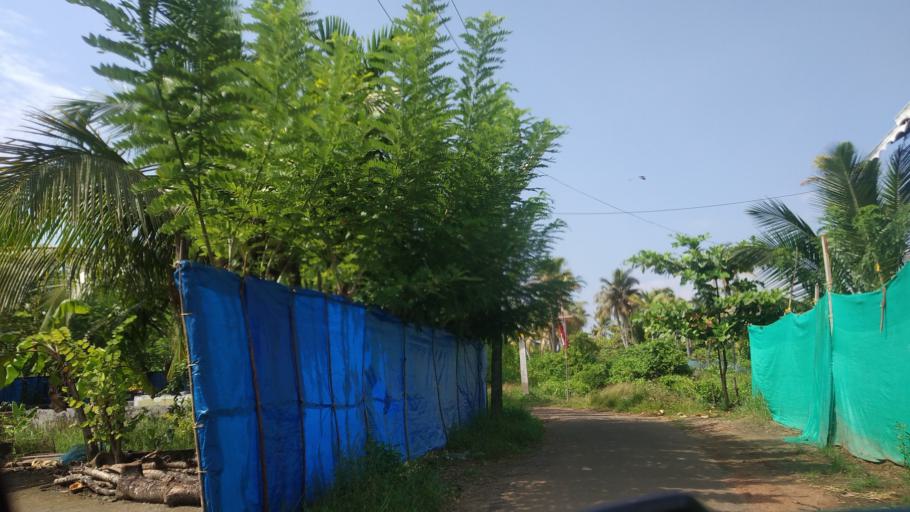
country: IN
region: Kerala
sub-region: Ernakulam
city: Elur
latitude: 10.0819
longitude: 76.2030
